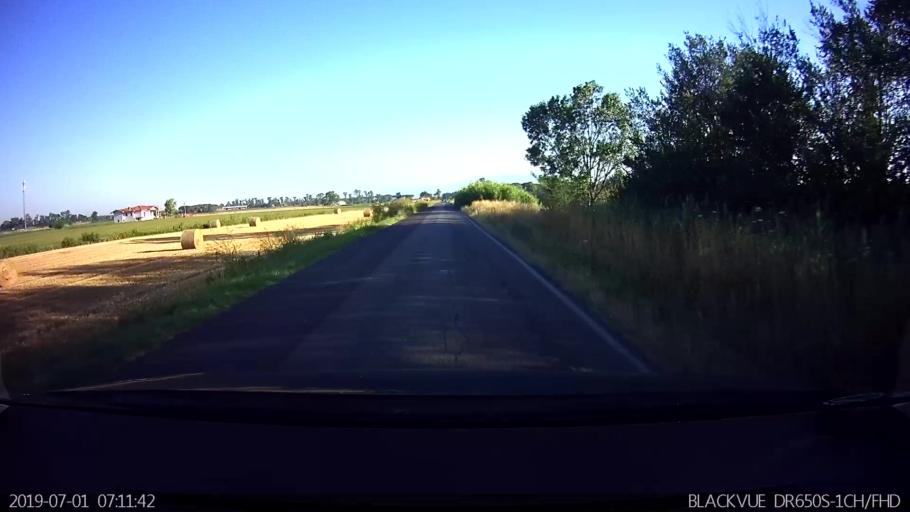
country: IT
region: Latium
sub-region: Provincia di Latina
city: Borgo Hermada
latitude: 41.3228
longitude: 13.1769
